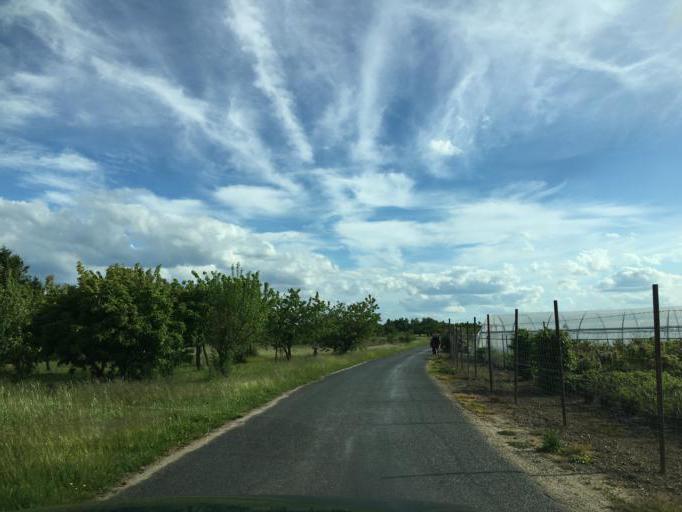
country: FR
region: Centre
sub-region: Departement du Loiret
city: Mareau-aux-Pres
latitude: 47.8408
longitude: 1.8071
